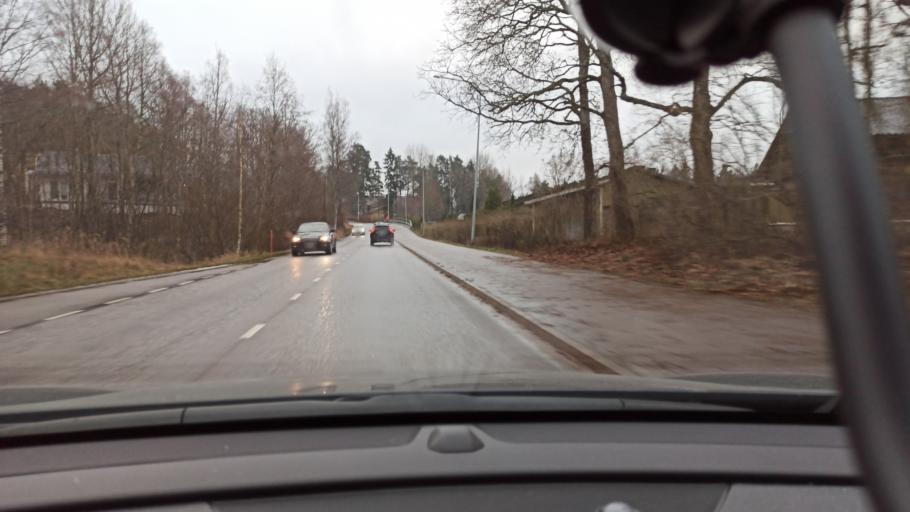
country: FI
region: Uusimaa
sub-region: Helsinki
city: Kirkkonummi
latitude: 60.1323
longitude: 24.4302
